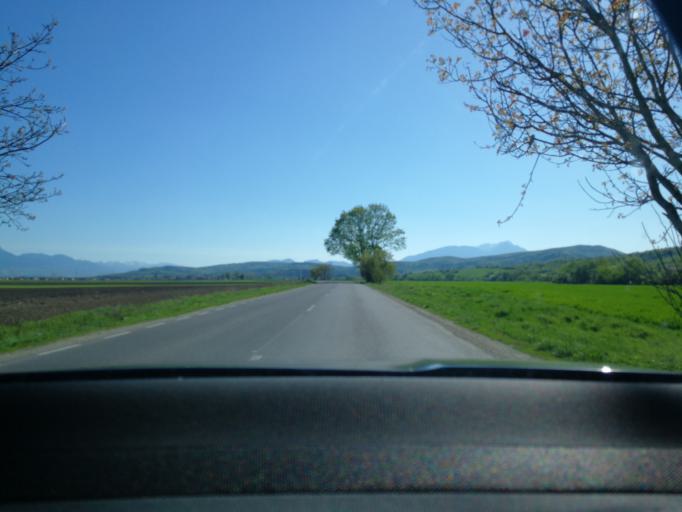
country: RO
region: Brasov
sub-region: Comuna Vulcan
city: Vulcan
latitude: 45.6516
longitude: 25.4317
